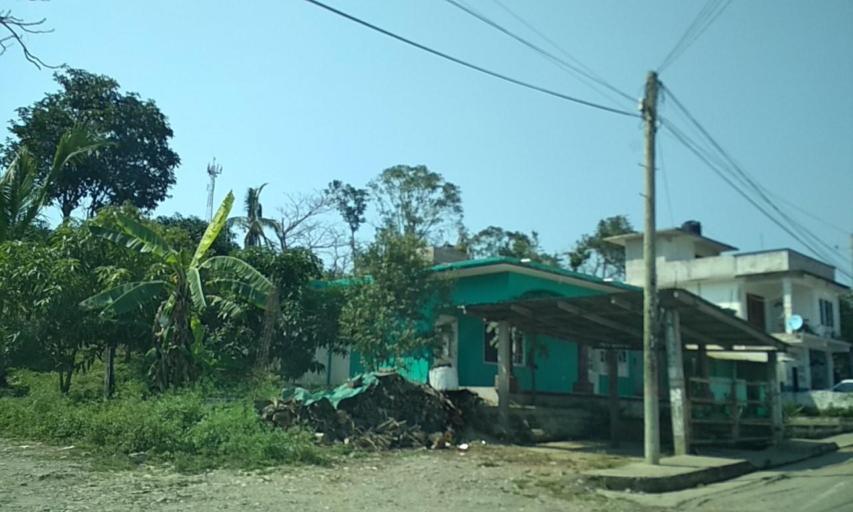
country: MX
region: Veracruz
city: Agua Dulce
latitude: 20.3710
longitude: -97.1777
